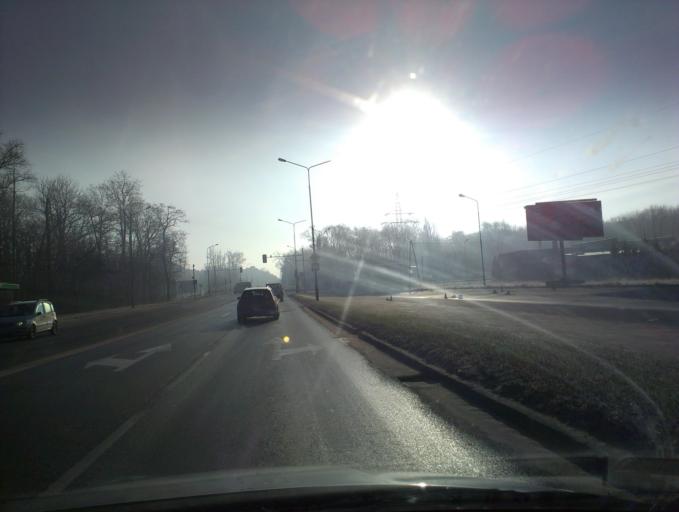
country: PL
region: Greater Poland Voivodeship
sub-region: Poznan
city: Poznan
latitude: 52.3990
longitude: 16.9731
